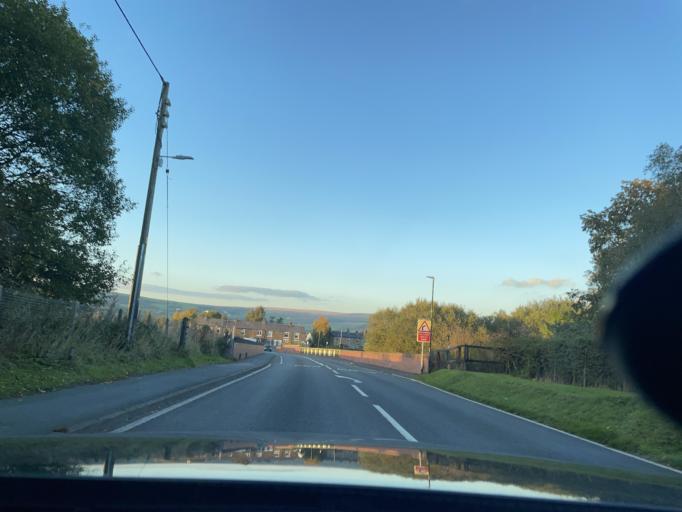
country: GB
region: England
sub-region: Borough of Tameside
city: Longdendale
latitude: 53.4419
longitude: -1.9878
